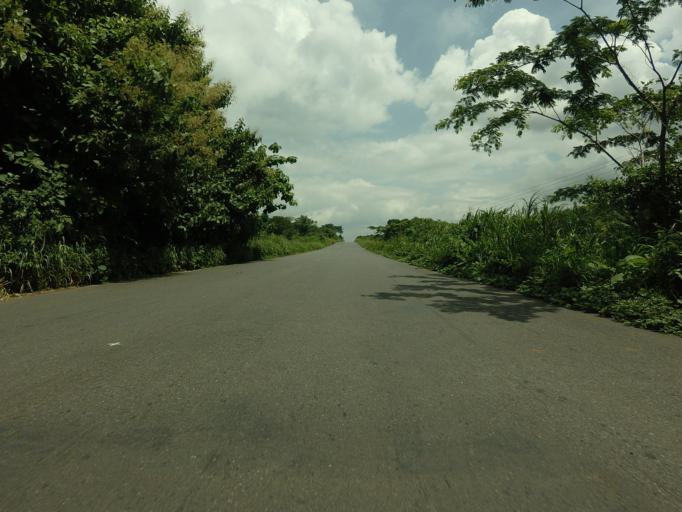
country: GH
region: Volta
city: Ho
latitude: 6.5751
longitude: 0.2767
